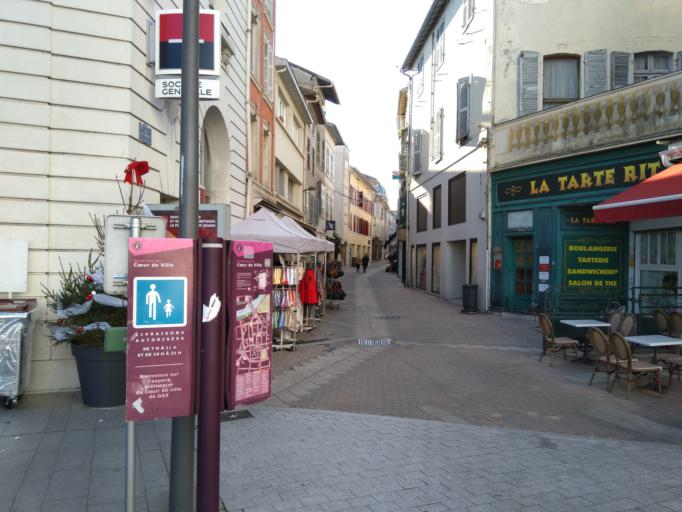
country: FR
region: Aquitaine
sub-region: Departement des Landes
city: Dax
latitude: 43.7110
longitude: -1.0543
